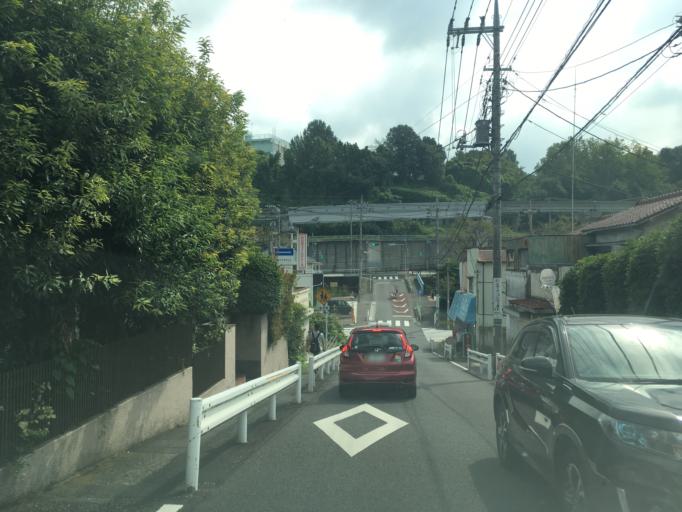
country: JP
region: Tokyo
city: Hino
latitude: 35.6536
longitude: 139.4078
